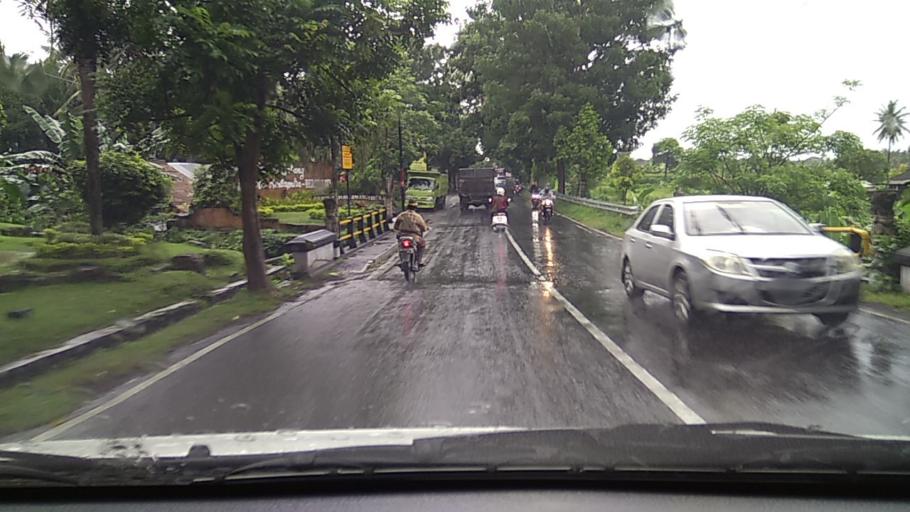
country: ID
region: Bali
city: Banjar Timbrah
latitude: -8.4791
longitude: 115.6126
